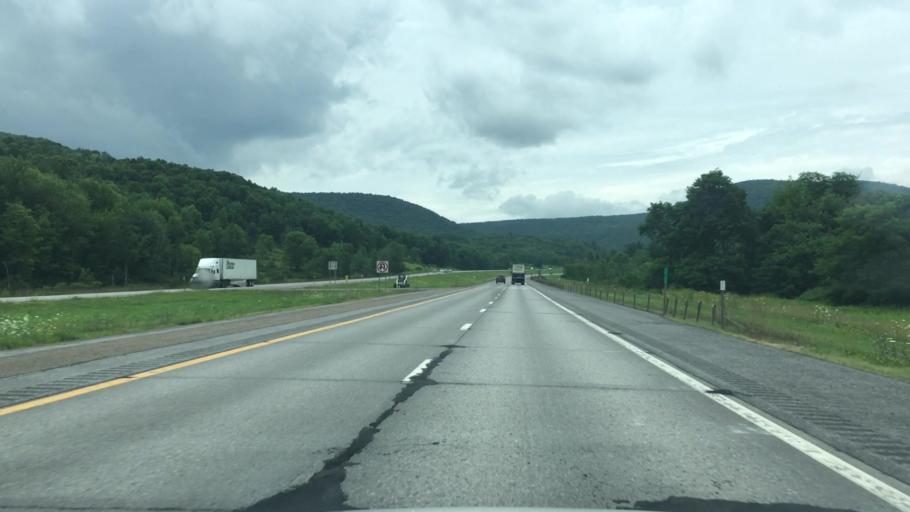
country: US
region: New York
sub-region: Schoharie County
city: Cobleskill
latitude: 42.6492
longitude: -74.6083
